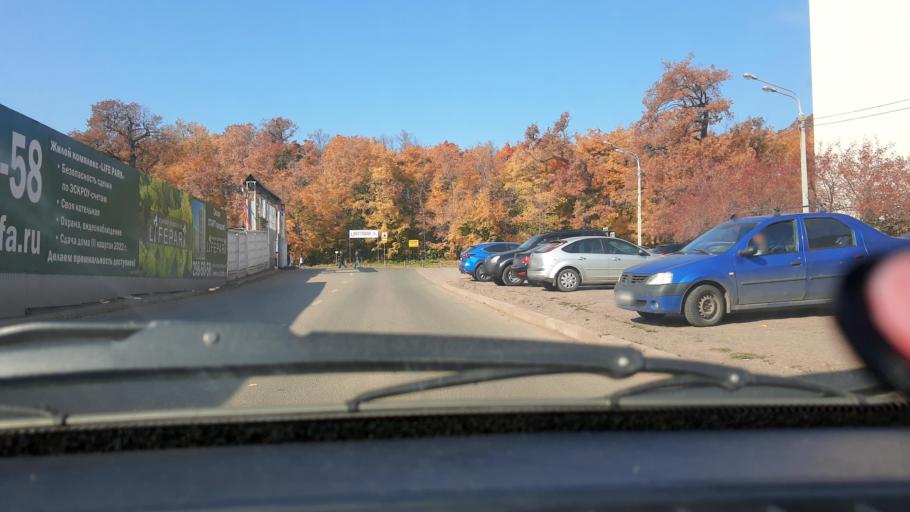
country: RU
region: Bashkortostan
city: Ufa
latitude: 54.7532
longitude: 55.9866
